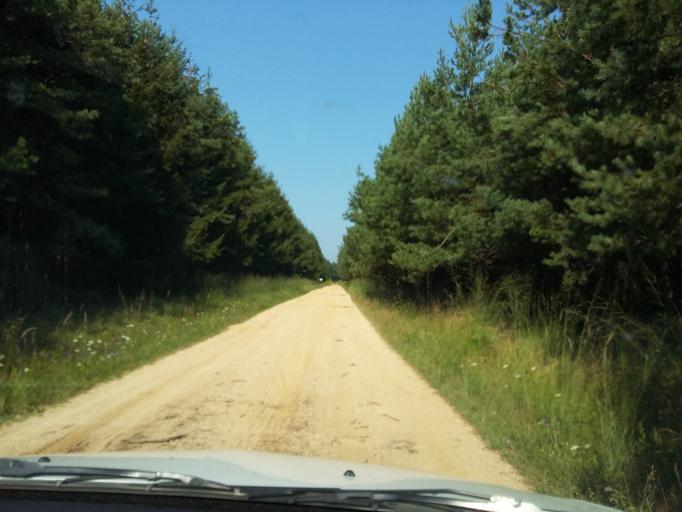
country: SI
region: Hodos-Hodos
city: Hodos
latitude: 46.8573
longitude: 16.3204
